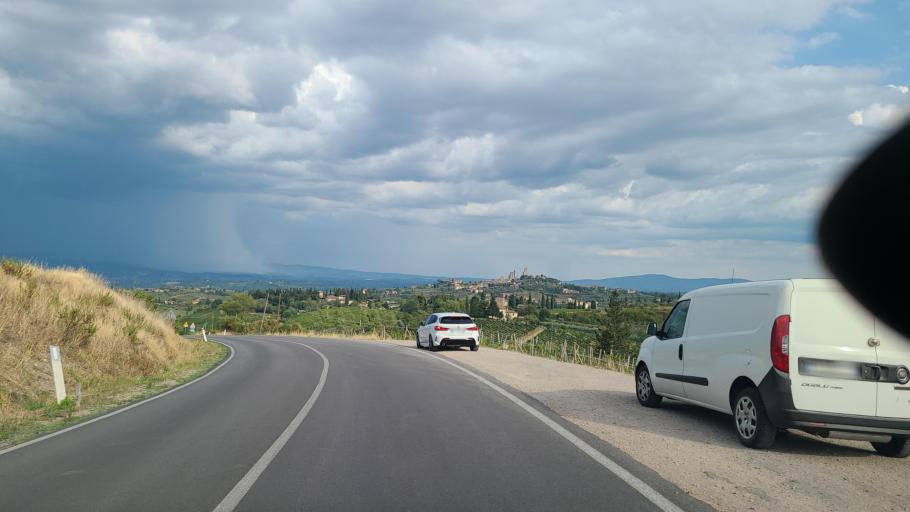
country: IT
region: Tuscany
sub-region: Provincia di Siena
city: San Gimignano
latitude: 43.4805
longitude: 11.0129
